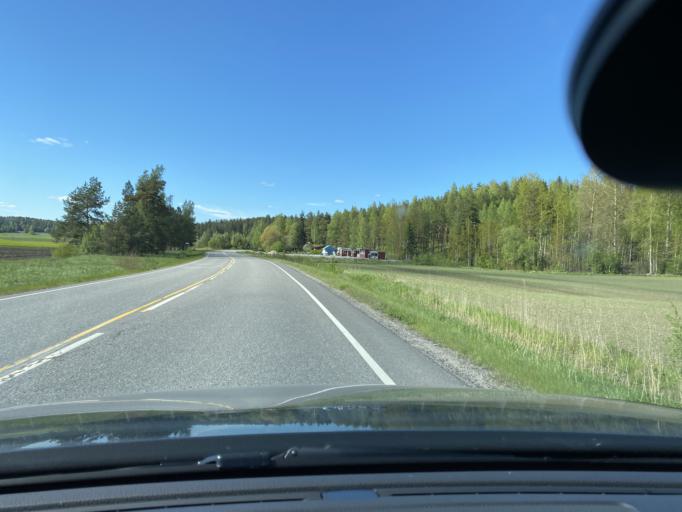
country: FI
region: Varsinais-Suomi
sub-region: Turku
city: Sauvo
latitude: 60.3687
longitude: 22.6735
